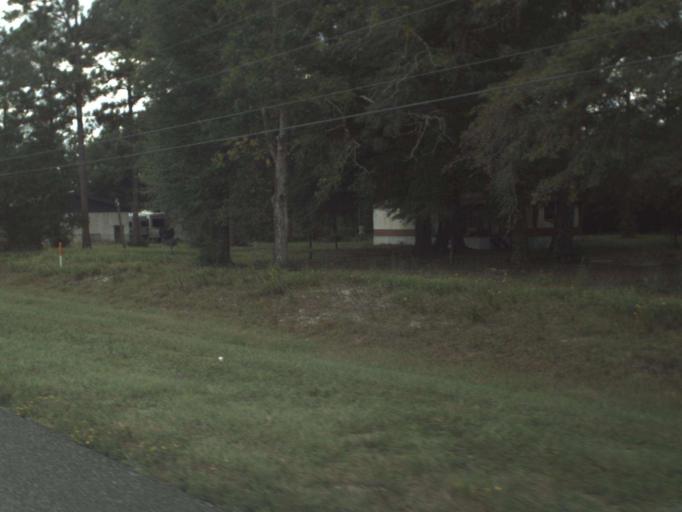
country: US
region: Florida
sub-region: Bay County
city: Youngstown
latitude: 30.4603
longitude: -85.4238
